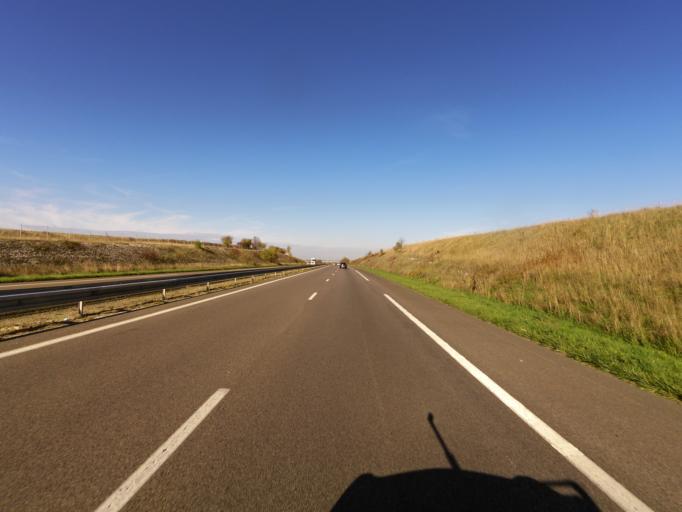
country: FR
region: Champagne-Ardenne
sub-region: Departement de la Marne
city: Verzy
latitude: 49.1428
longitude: 4.2141
